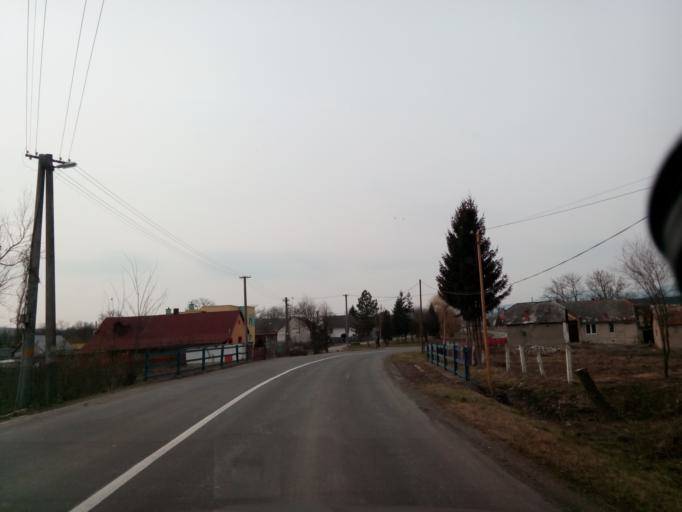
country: SK
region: Kosicky
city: Secovce
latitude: 48.6122
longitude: 21.6122
